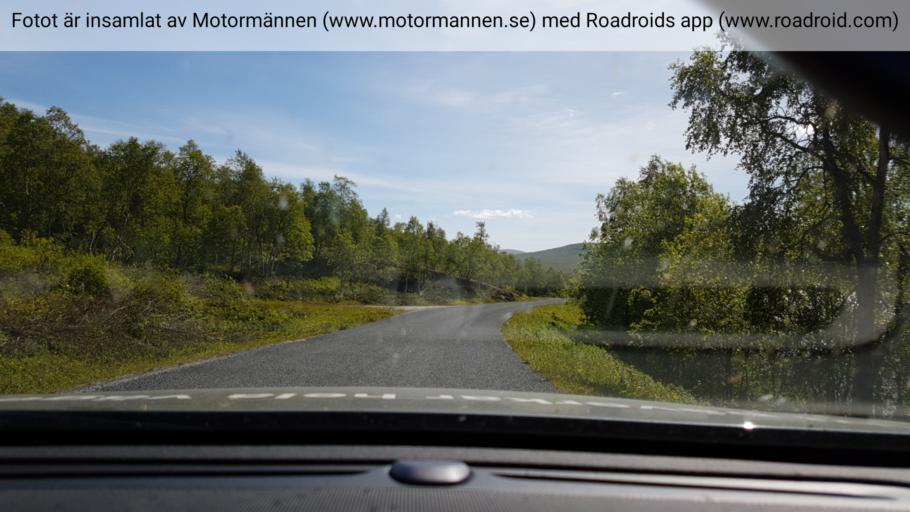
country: NO
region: Nordland
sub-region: Hattfjelldal
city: Hattfjelldal
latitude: 65.4180
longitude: 14.7132
